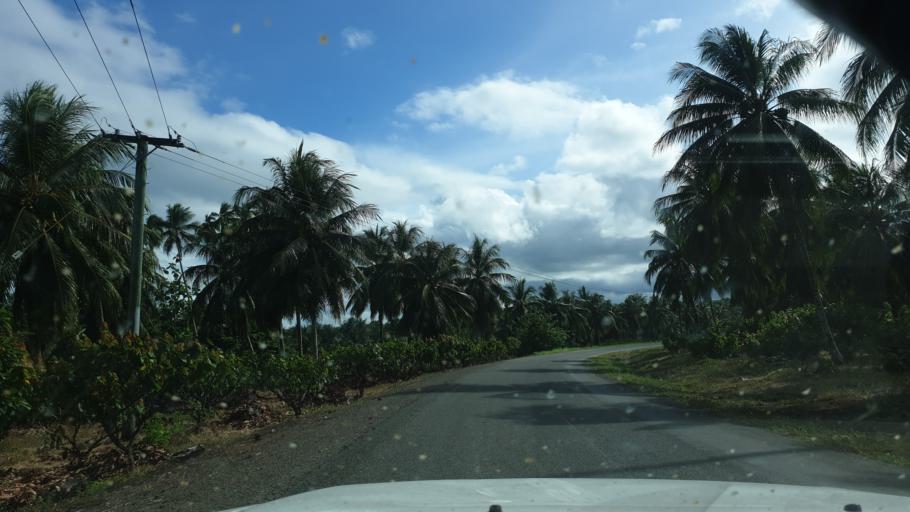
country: PG
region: Madang
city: Madang
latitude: -4.9724
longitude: 145.7801
